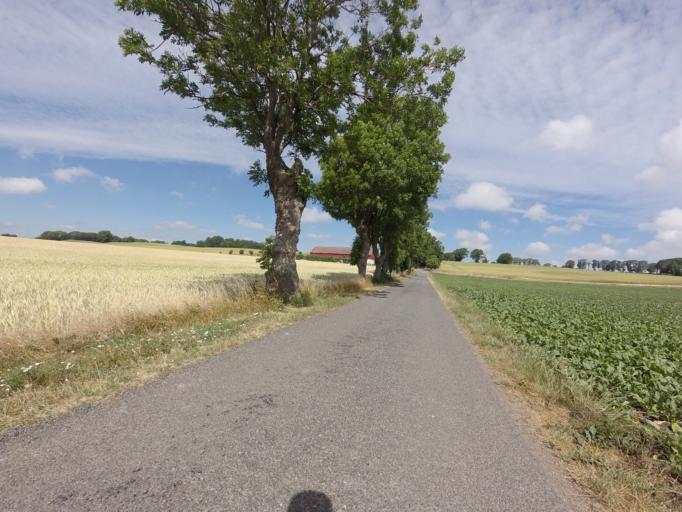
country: SE
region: Skane
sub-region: Simrishamns Kommun
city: Simrishamn
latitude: 55.4898
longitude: 14.3098
